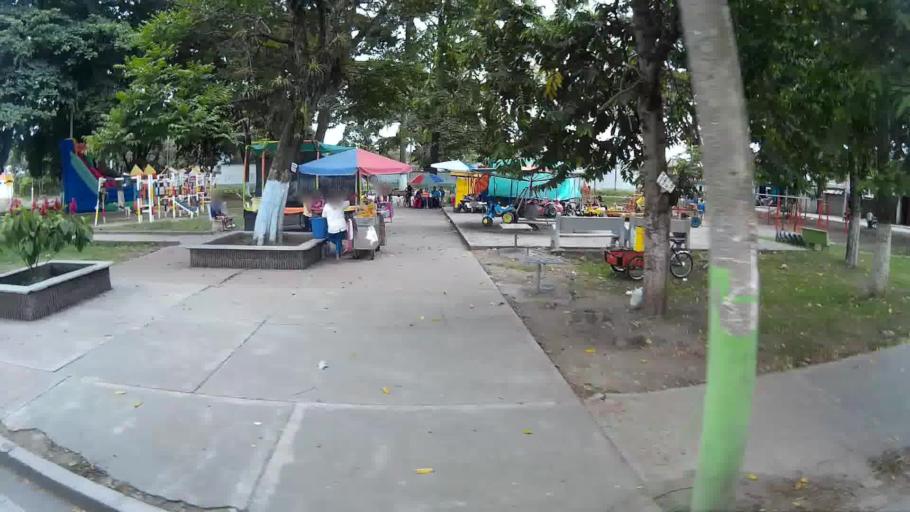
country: CO
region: Risaralda
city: La Virginia
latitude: 4.9015
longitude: -75.8844
